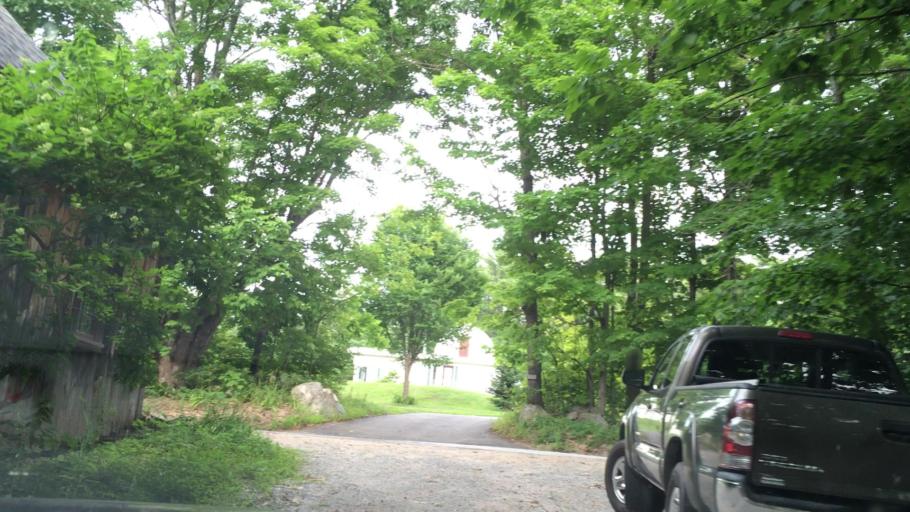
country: US
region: New Hampshire
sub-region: Belknap County
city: Meredith
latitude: 43.6969
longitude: -71.5101
